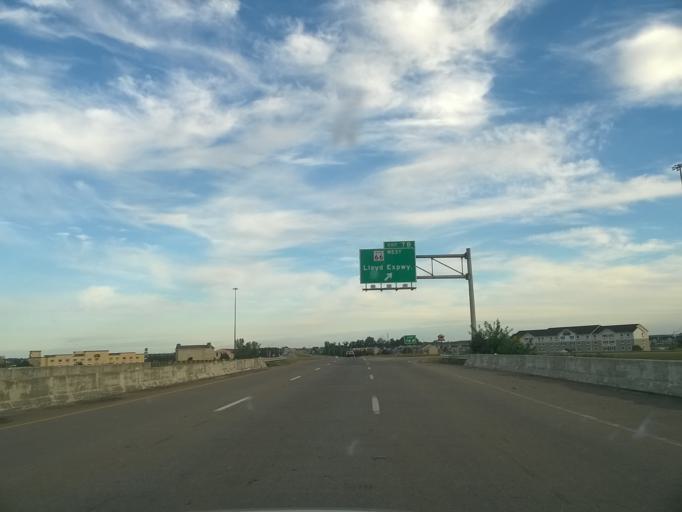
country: US
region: Indiana
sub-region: Warrick County
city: Newburgh
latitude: 37.9776
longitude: -87.4522
